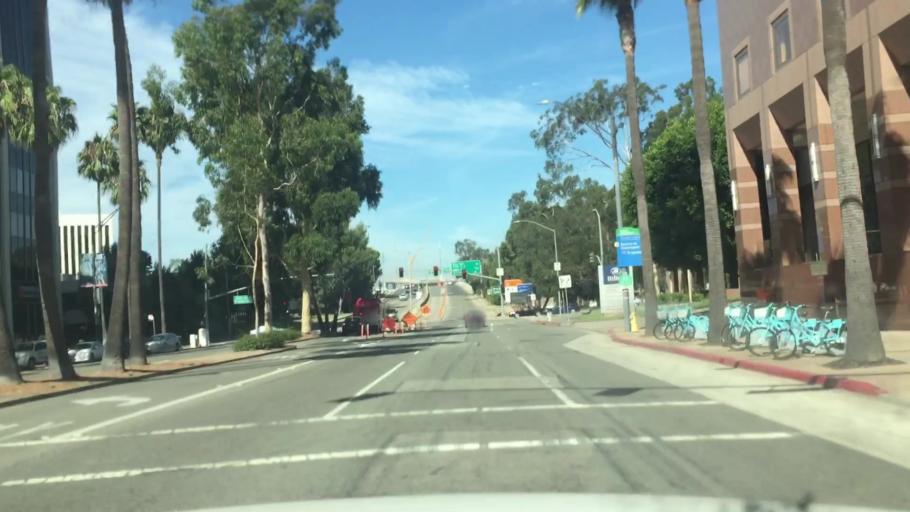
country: US
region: California
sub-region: Los Angeles County
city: Long Beach
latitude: 33.7674
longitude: -118.2006
